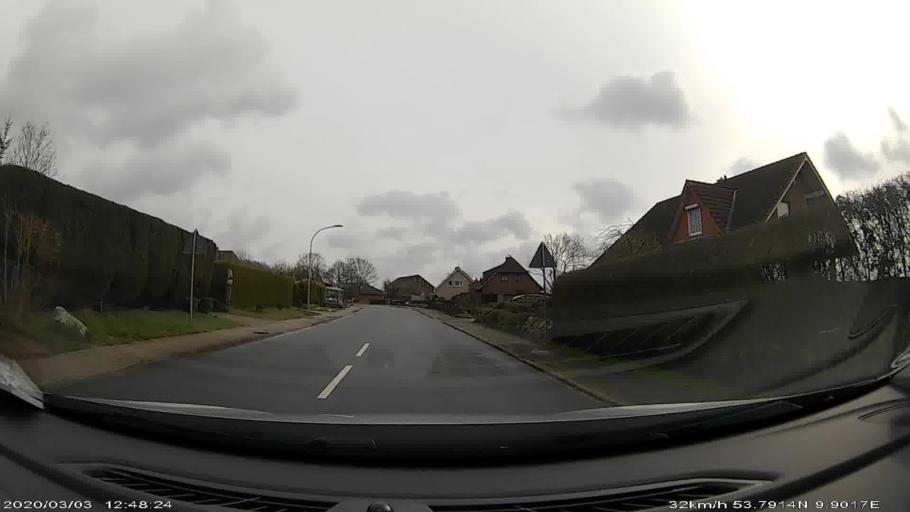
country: DE
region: Schleswig-Holstein
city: Alveslohe
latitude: 53.7909
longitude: 9.9031
